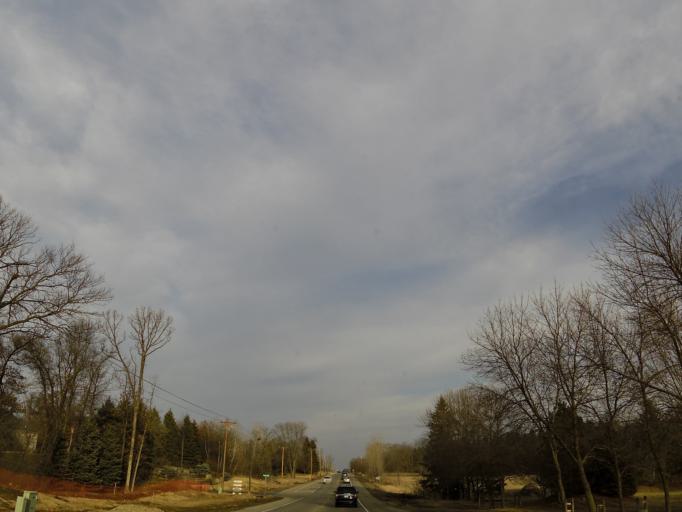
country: US
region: Minnesota
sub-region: Dakota County
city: Lakeville
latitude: 44.6813
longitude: -93.2712
